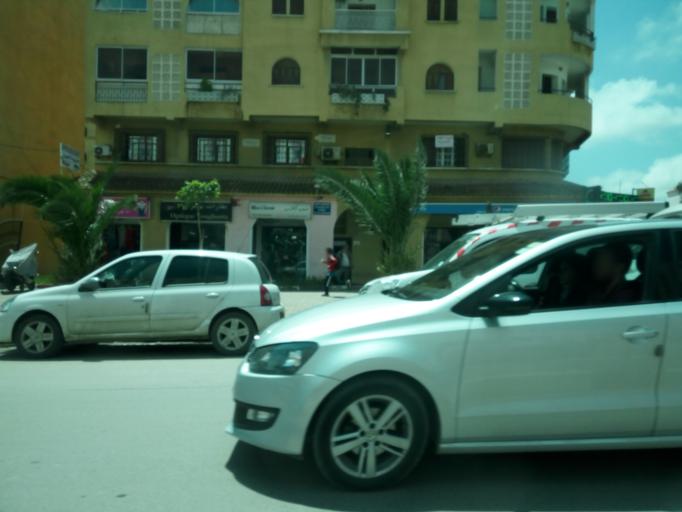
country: DZ
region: Tipaza
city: Saoula
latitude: 36.7221
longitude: 2.9926
